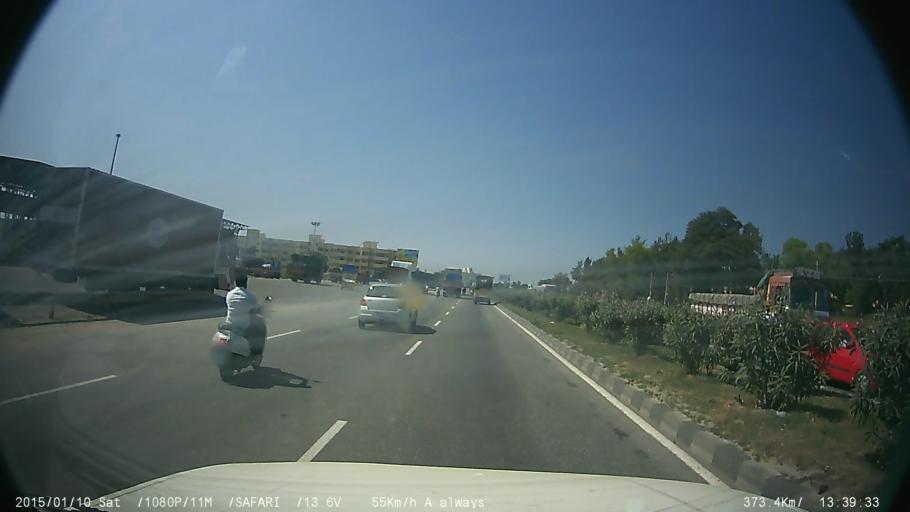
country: IN
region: Tamil Nadu
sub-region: Krishnagiri
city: Hosur
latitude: 12.7810
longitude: 77.7643
